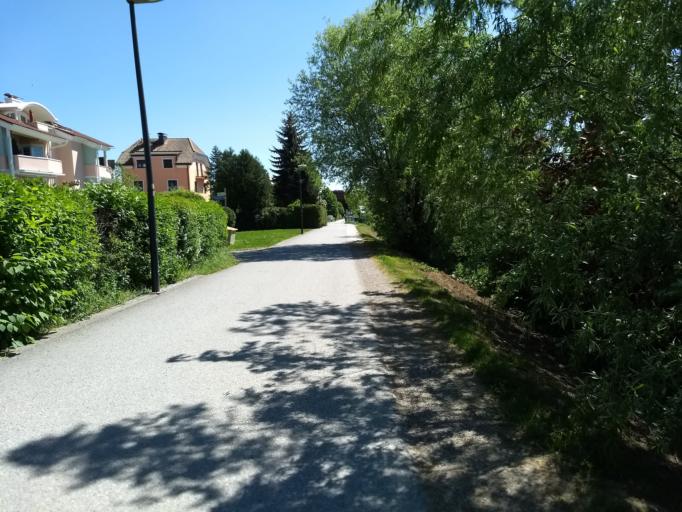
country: AT
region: Salzburg
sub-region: Politischer Bezirk Salzburg-Umgebung
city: Bergheim
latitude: 47.8243
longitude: 13.0334
